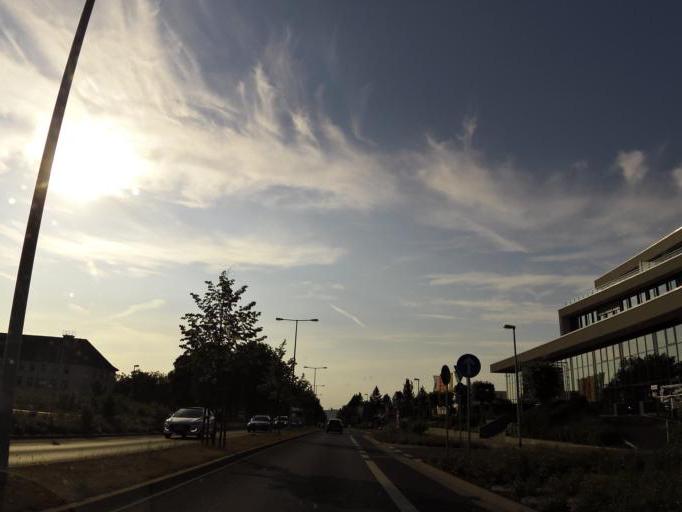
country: DE
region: Bavaria
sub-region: Regierungsbezirk Unterfranken
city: Aschaffenburg
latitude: 49.9640
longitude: 9.1736
